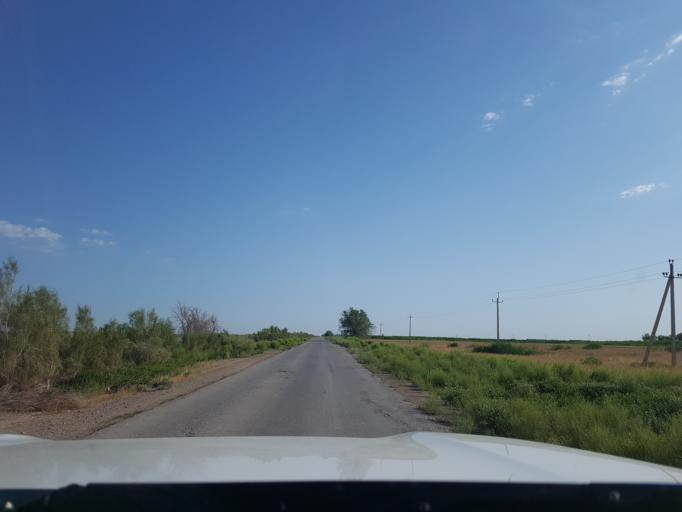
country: TM
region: Dasoguz
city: Koeneuergench
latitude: 41.9121
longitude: 58.7100
